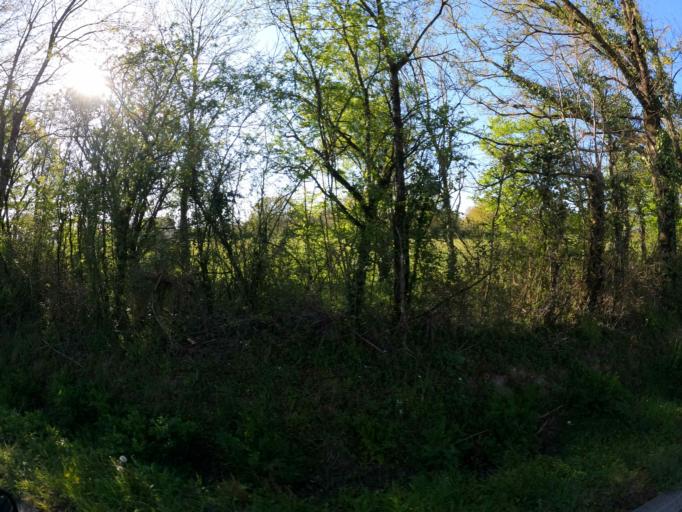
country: FR
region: Pays de la Loire
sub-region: Departement de la Vendee
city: Beaurepaire
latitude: 46.9161
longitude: -1.1231
